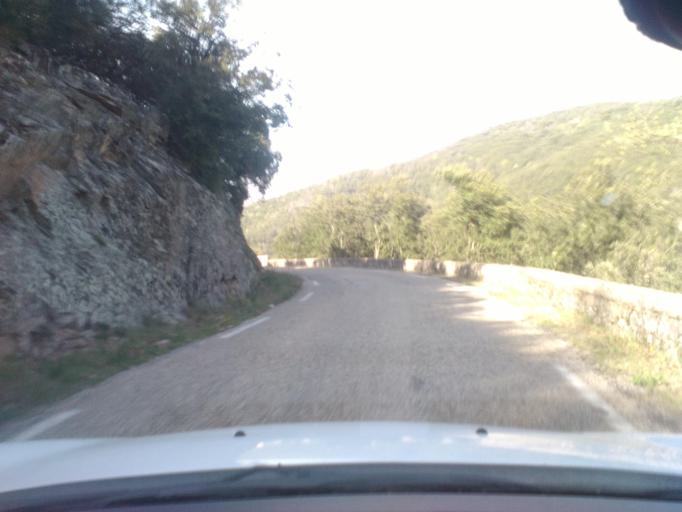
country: FR
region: Languedoc-Roussillon
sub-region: Departement du Gard
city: Lasalle
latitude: 44.0813
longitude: 3.8156
